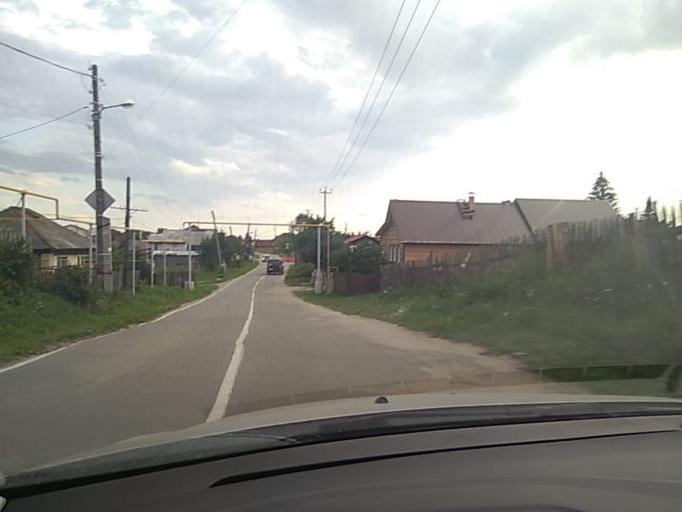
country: RU
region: Chelyabinsk
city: Kyshtym
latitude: 55.6959
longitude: 60.5316
